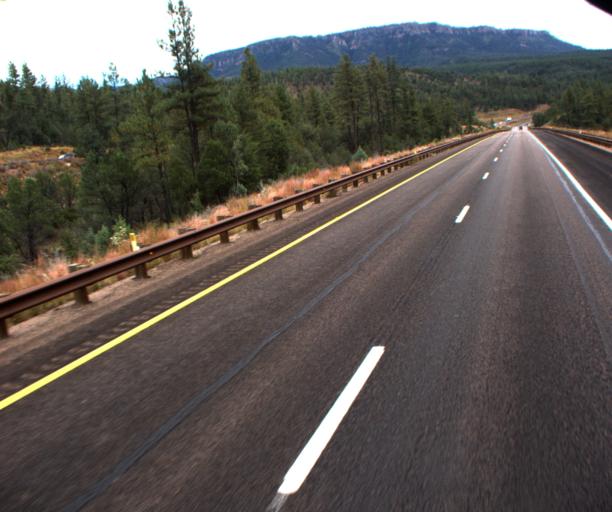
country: US
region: Arizona
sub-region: Gila County
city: Star Valley
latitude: 34.3272
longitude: -111.1003
